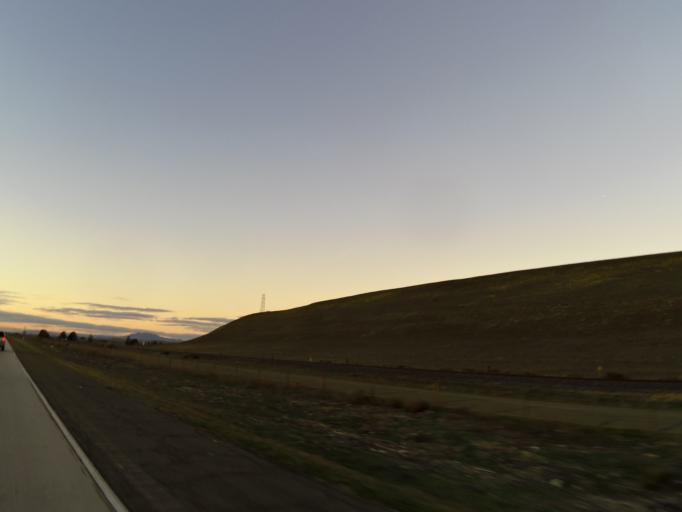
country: US
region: California
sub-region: Monterey County
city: King City
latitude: 36.1600
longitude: -121.0499
